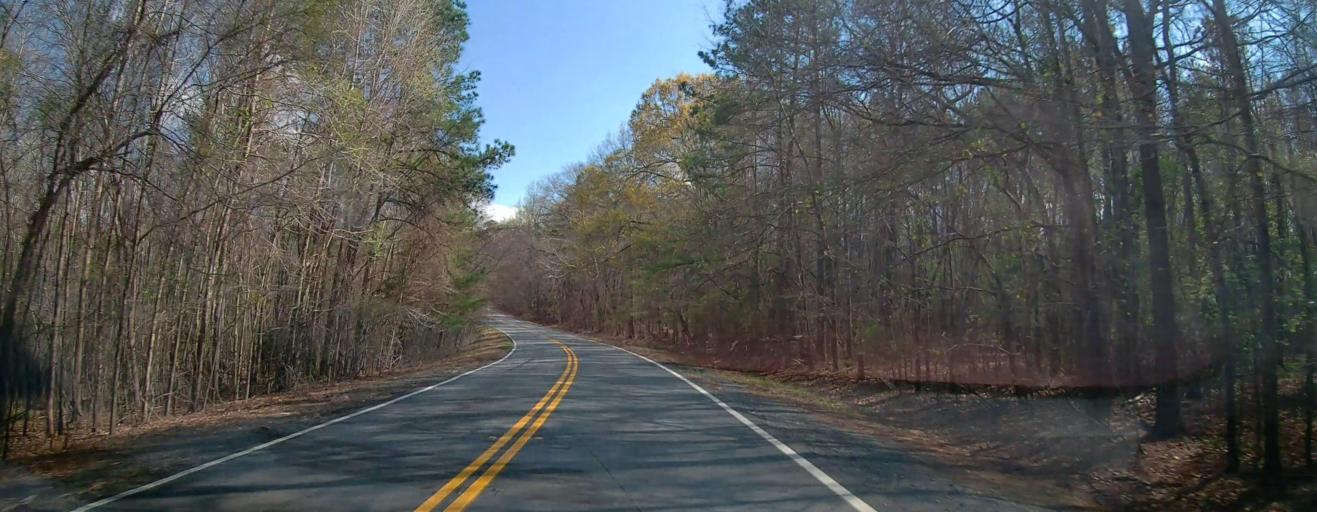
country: US
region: Georgia
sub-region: Twiggs County
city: Jeffersonville
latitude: 32.7272
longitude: -83.3494
